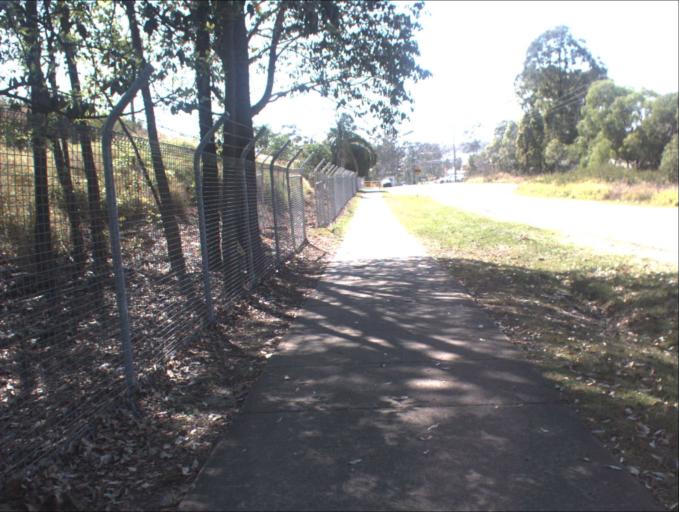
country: AU
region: Queensland
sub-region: Logan
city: Logan City
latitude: -27.6642
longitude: 153.1155
